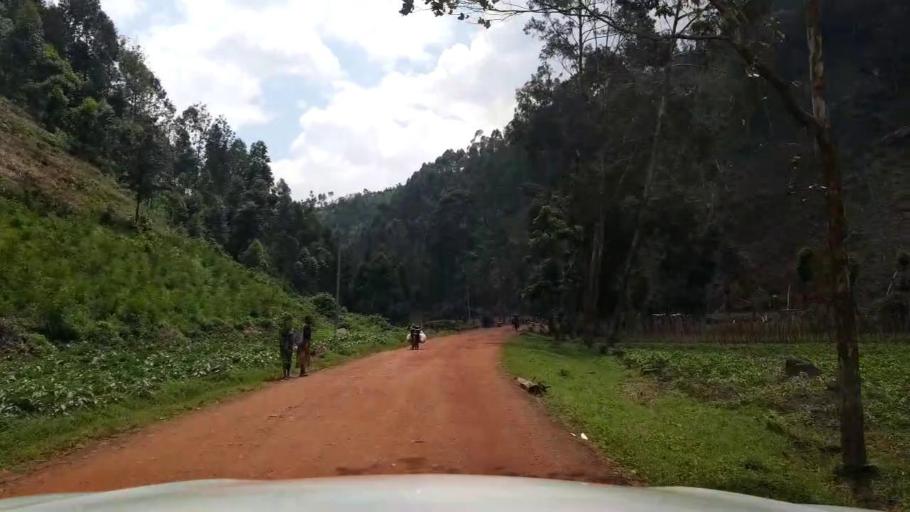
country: UG
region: Western Region
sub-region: Kisoro District
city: Kisoro
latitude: -1.3835
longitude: 29.7985
